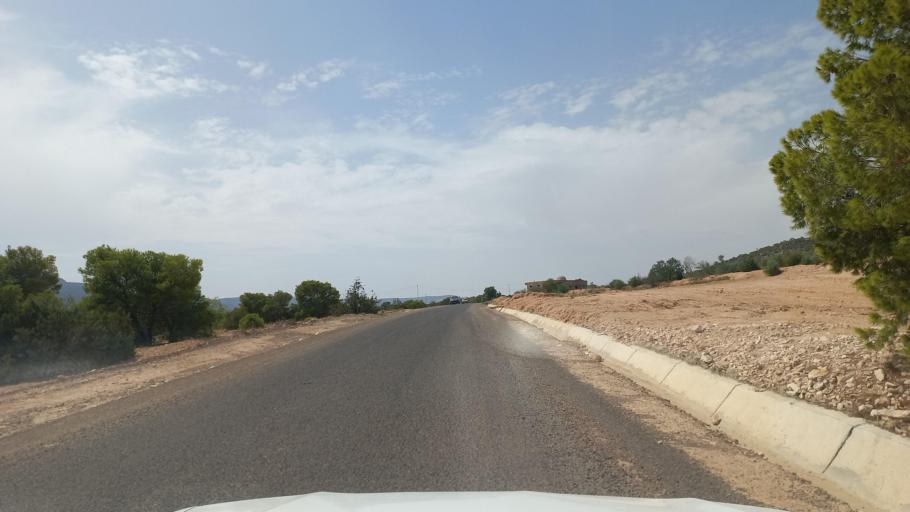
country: TN
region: Al Qasrayn
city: Kasserine
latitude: 35.3778
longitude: 8.9139
